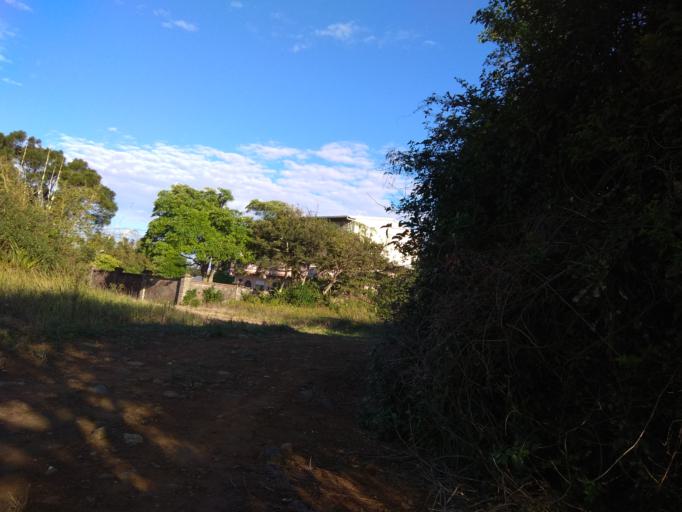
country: TW
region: Taiwan
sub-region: Hsinchu
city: Zhubei
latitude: 24.9874
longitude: 121.0364
